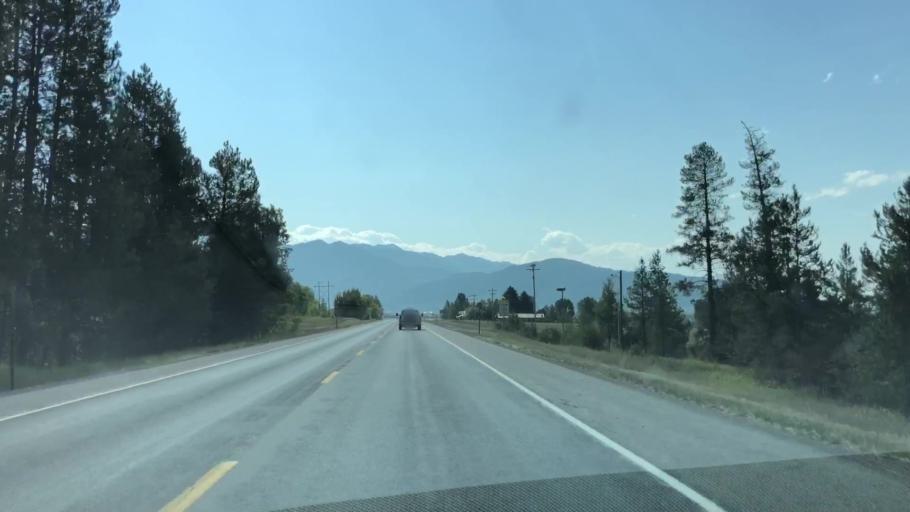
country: US
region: Wyoming
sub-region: Teton County
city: Hoback
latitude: 43.1960
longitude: -111.0399
